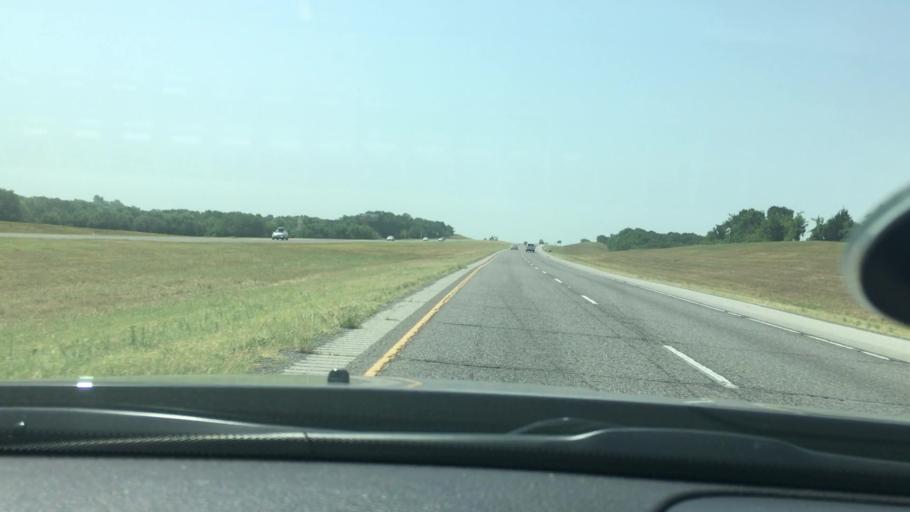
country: US
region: Oklahoma
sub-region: Garvin County
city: Wynnewood
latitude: 34.5841
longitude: -97.2034
